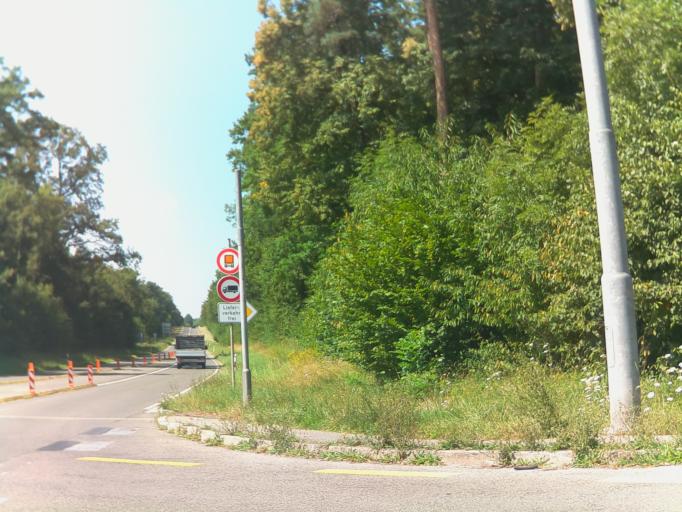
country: DE
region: Baden-Wuerttemberg
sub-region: Regierungsbezirk Stuttgart
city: Gerlingen
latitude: 48.7911
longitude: 9.0444
